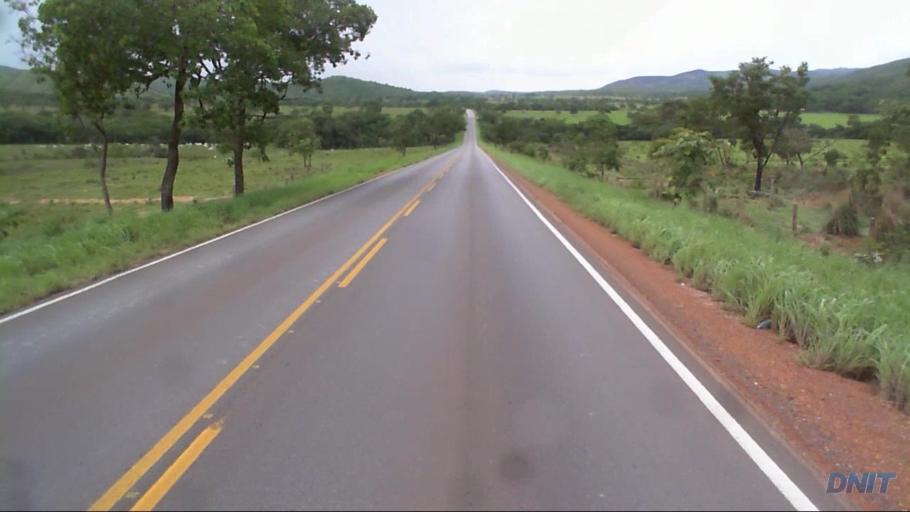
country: BR
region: Goias
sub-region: Padre Bernardo
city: Padre Bernardo
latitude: -15.4405
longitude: -48.1960
